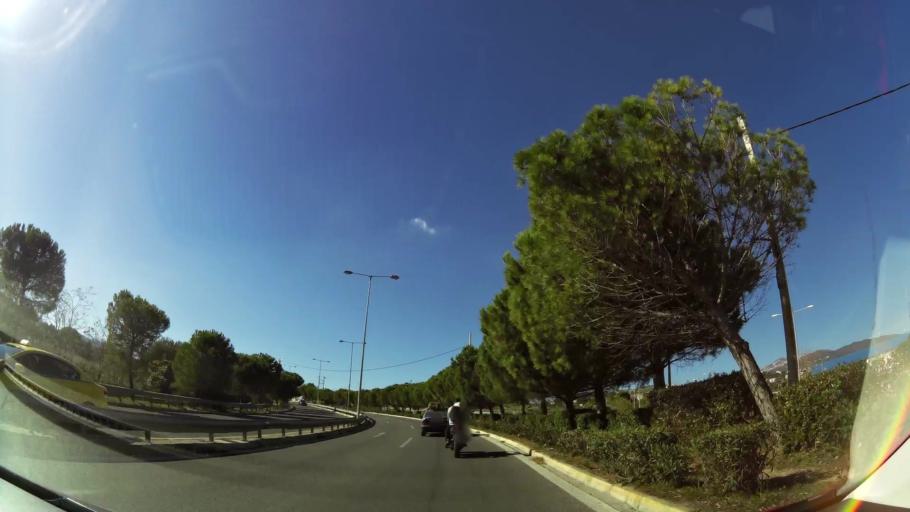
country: GR
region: Attica
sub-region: Nomarchia Anatolikis Attikis
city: Dhrafi
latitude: 38.0022
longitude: 23.9115
